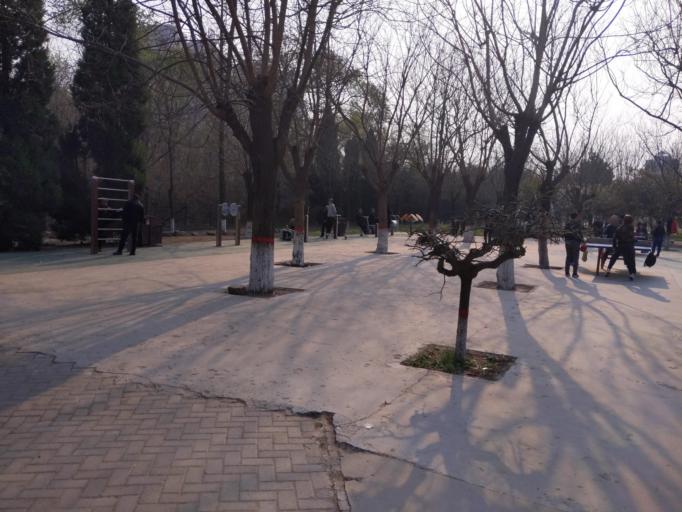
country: CN
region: Henan Sheng
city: Puyang
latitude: 35.7508
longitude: 115.0265
